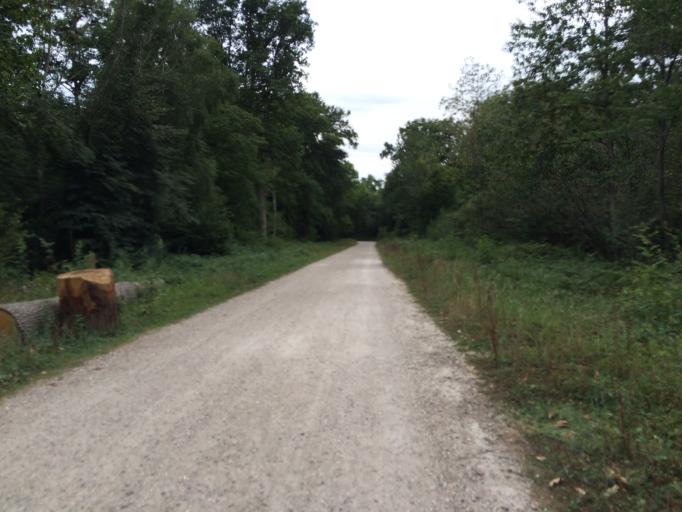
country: FR
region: Ile-de-France
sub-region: Departement de Seine-et-Marne
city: Lieusaint
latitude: 48.6479
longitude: 2.5353
